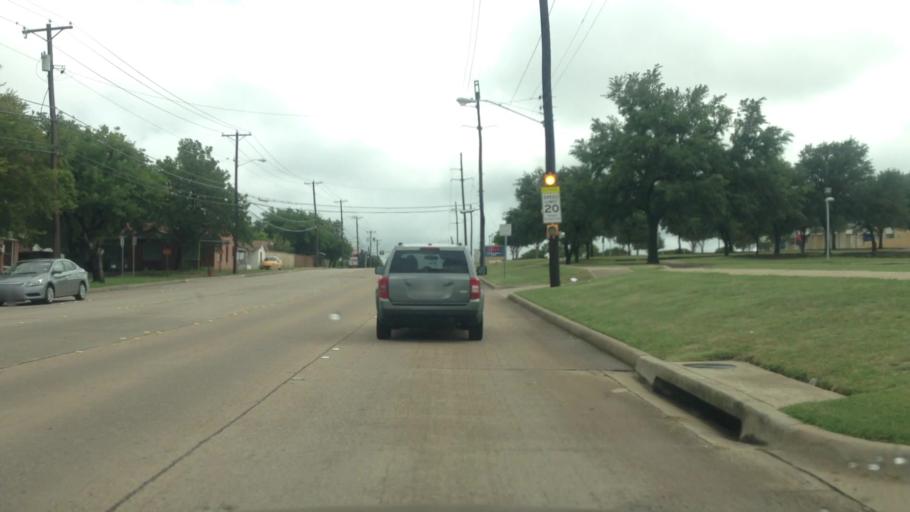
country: US
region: Texas
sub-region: Tarrant County
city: White Settlement
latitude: 32.7503
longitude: -97.4518
